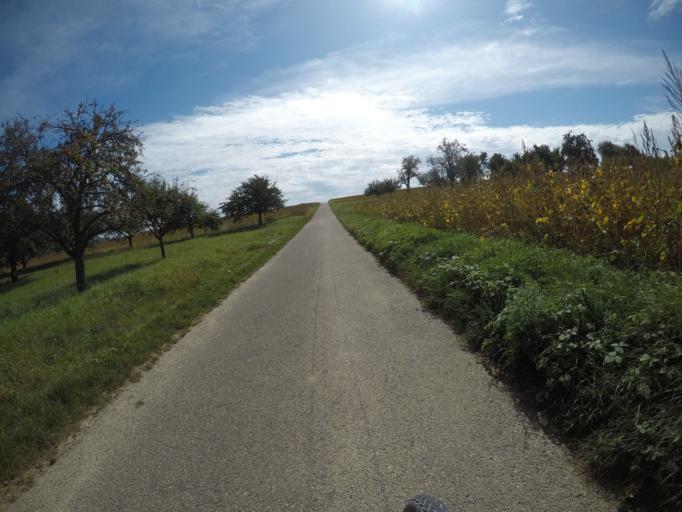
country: DE
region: Baden-Wuerttemberg
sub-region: Karlsruhe Region
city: Oberderdingen
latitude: 49.0808
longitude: 8.7926
